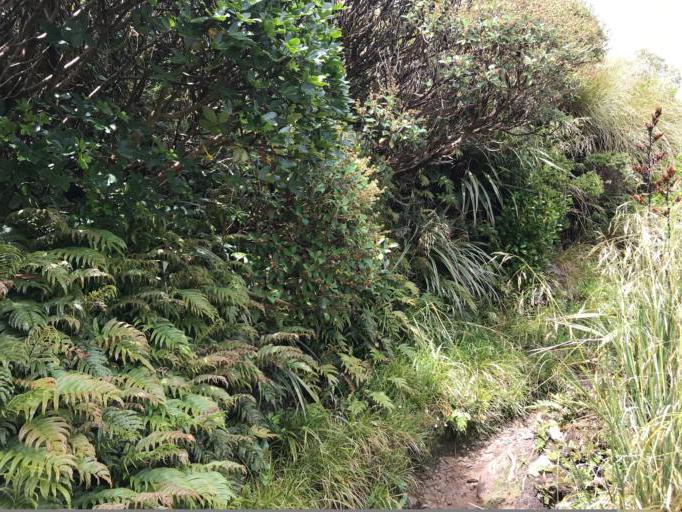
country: NZ
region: Wellington
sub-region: Kapiti Coast District
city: Otaki
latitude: -40.9111
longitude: 175.2611
